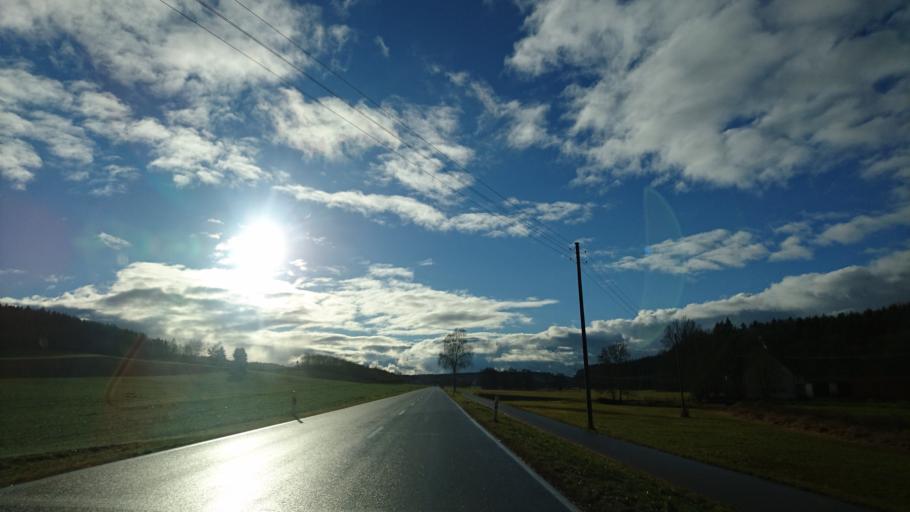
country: DE
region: Bavaria
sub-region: Swabia
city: Biberbach
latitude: 48.5030
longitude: 10.7935
